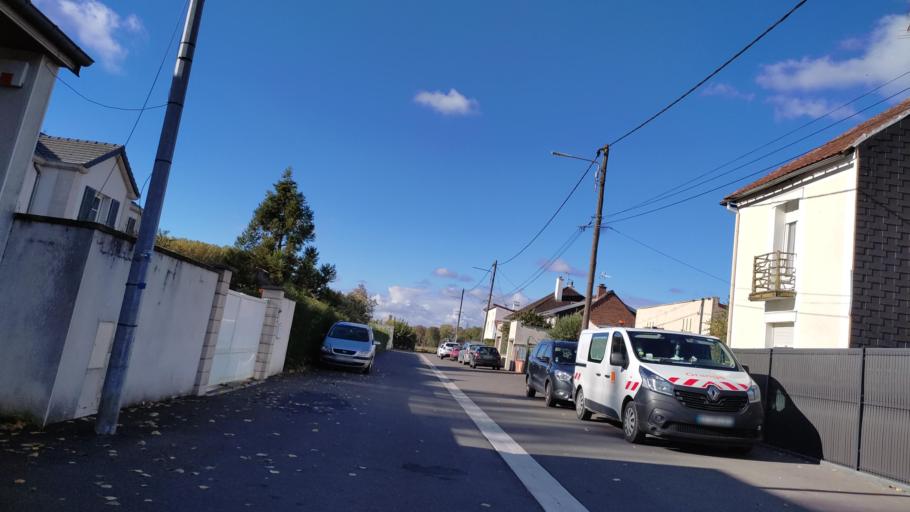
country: FR
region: Nord-Pas-de-Calais
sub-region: Departement du Pas-de-Calais
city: Saint-Nicolas
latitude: 50.3009
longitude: 2.7741
